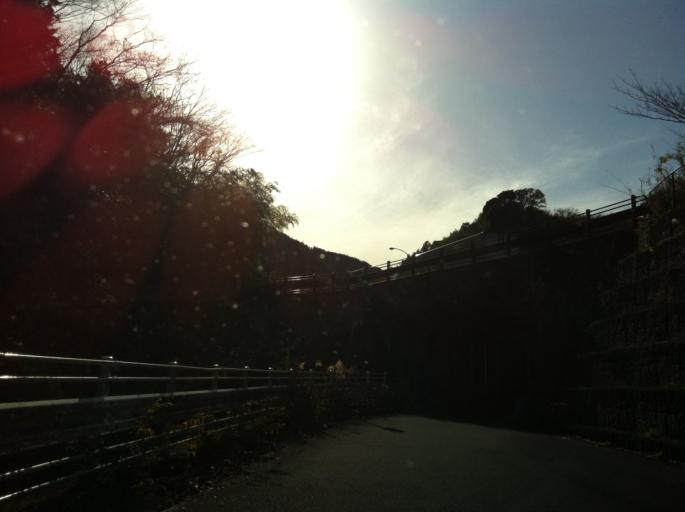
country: JP
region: Shizuoka
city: Yaizu
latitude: 34.9282
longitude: 138.3026
